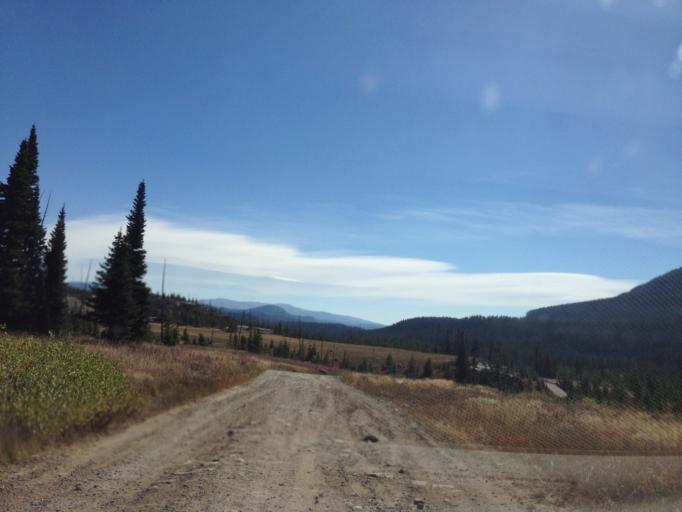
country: US
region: Montana
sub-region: Stillwater County
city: Absarokee
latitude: 45.0322
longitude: -109.9058
